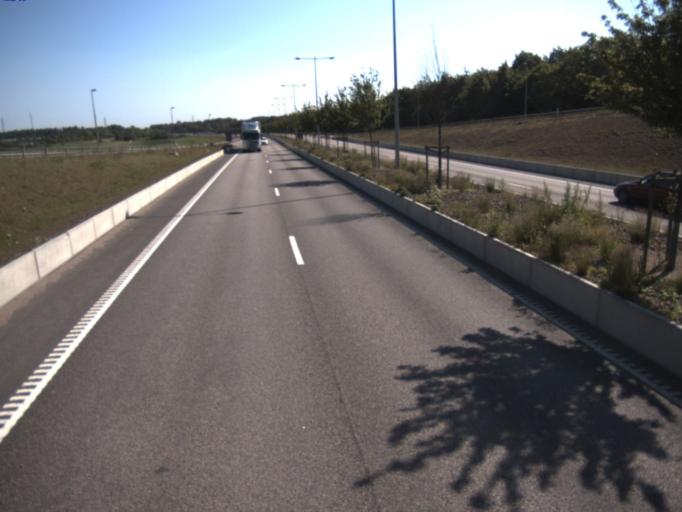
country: SE
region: Skane
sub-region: Helsingborg
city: Gantofta
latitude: 56.0268
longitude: 12.7612
